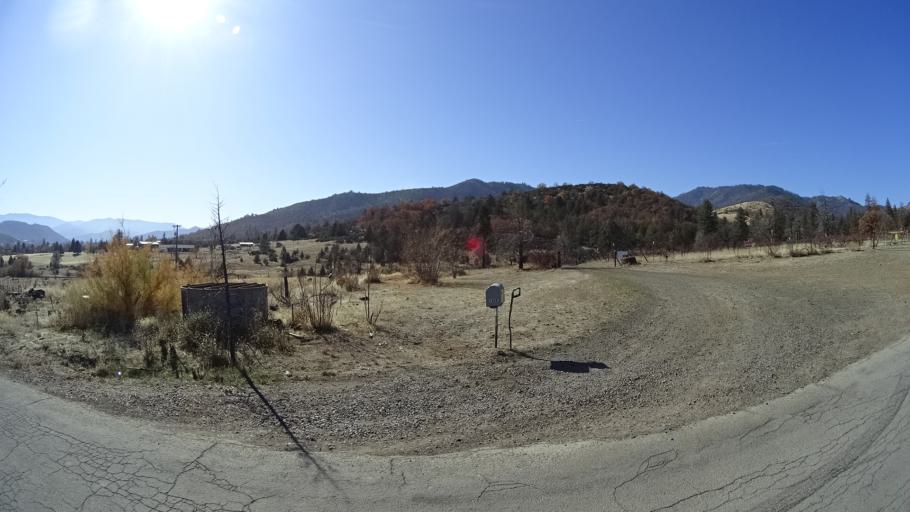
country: US
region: California
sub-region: Siskiyou County
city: Yreka
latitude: 41.7643
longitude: -122.6271
